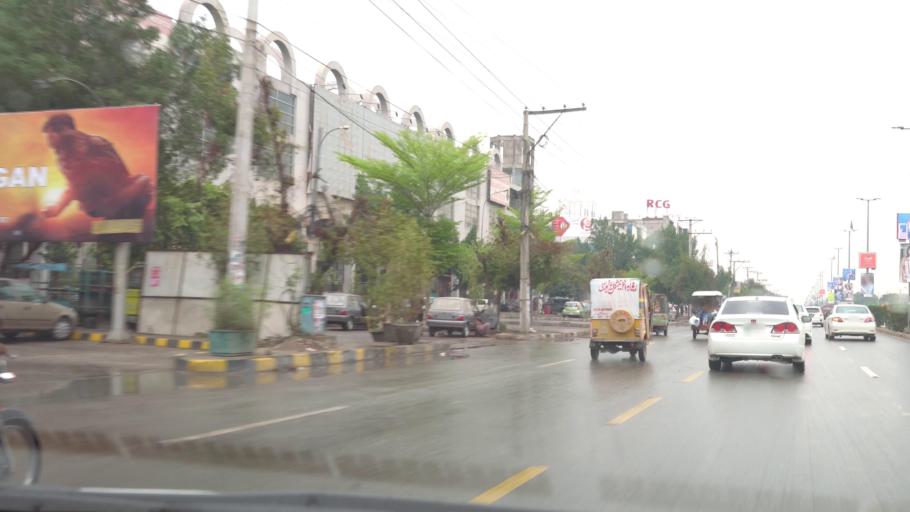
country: PK
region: Punjab
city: Faisalabad
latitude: 31.4163
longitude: 73.1093
